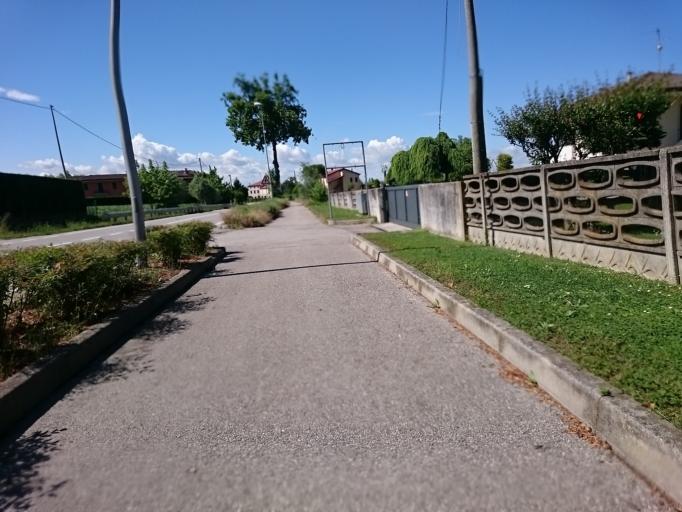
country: IT
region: Veneto
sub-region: Provincia di Venezia
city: Campolongo Maggiore
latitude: 45.3180
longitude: 12.0355
